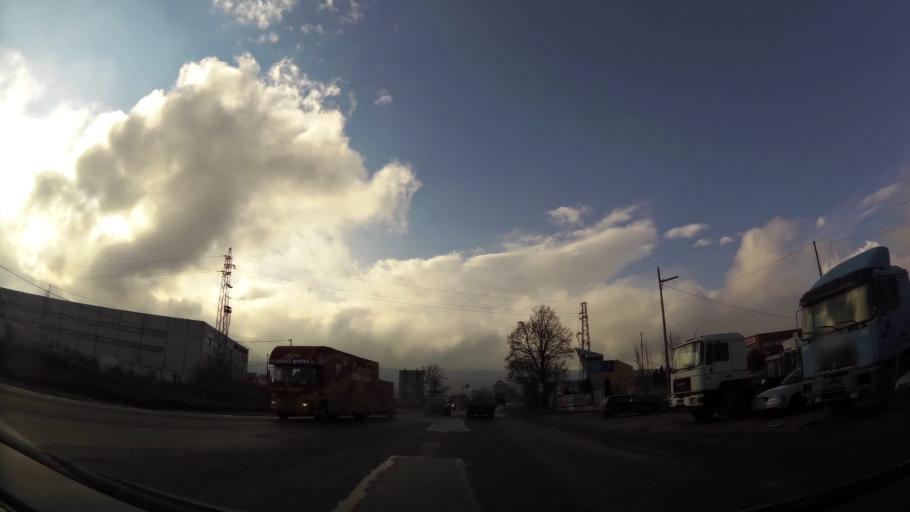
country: BG
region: Sofia-Capital
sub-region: Stolichna Obshtina
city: Sofia
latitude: 42.6278
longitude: 23.4462
